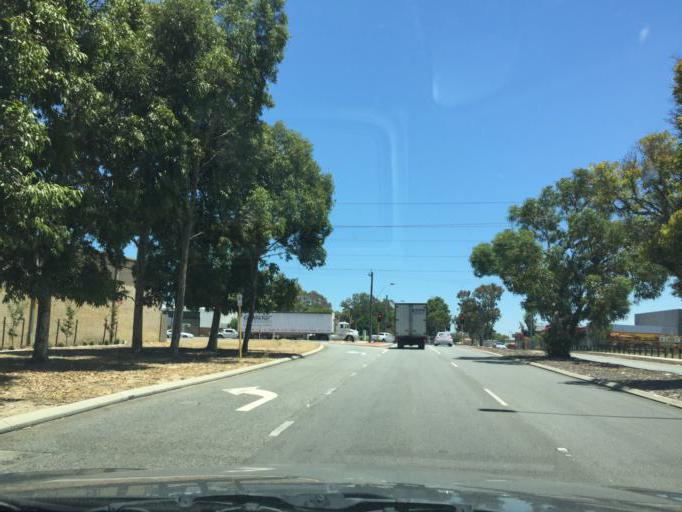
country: AU
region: Western Australia
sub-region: Canning
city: Canning Vale
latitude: -32.0616
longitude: 115.9229
